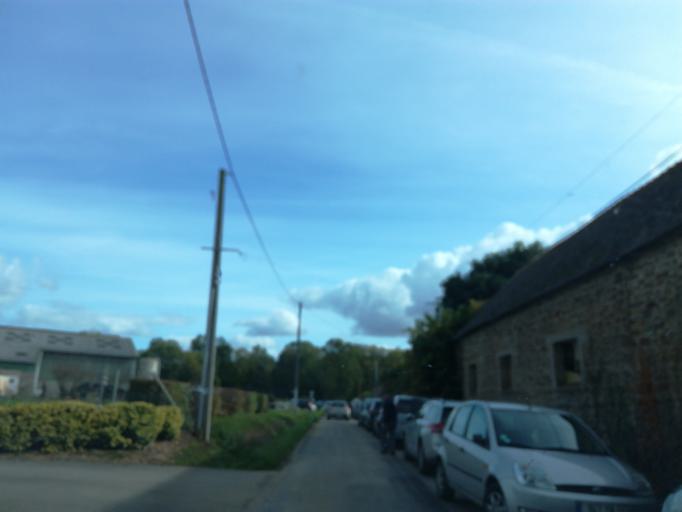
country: FR
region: Brittany
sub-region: Departement du Morbihan
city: Rohan
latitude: 48.0901
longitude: -2.7712
